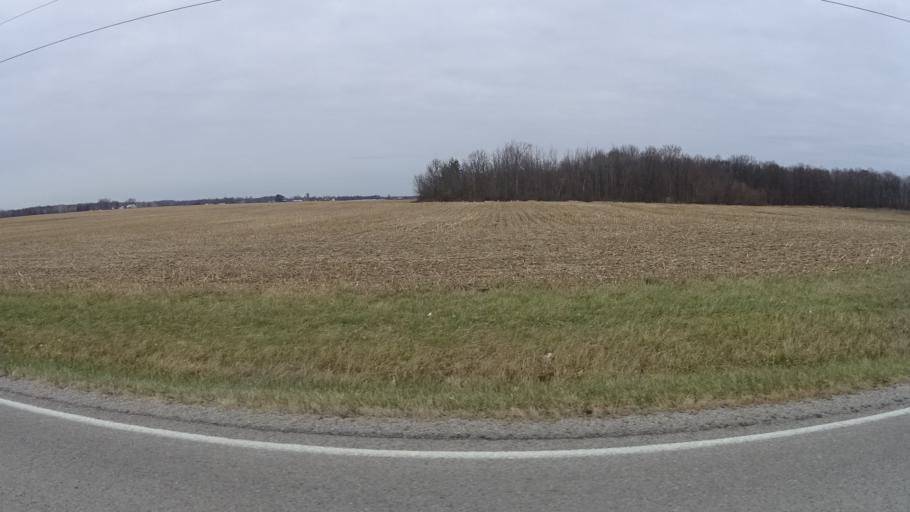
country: US
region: Ohio
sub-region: Lorain County
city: Wellington
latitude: 41.1999
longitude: -82.1919
